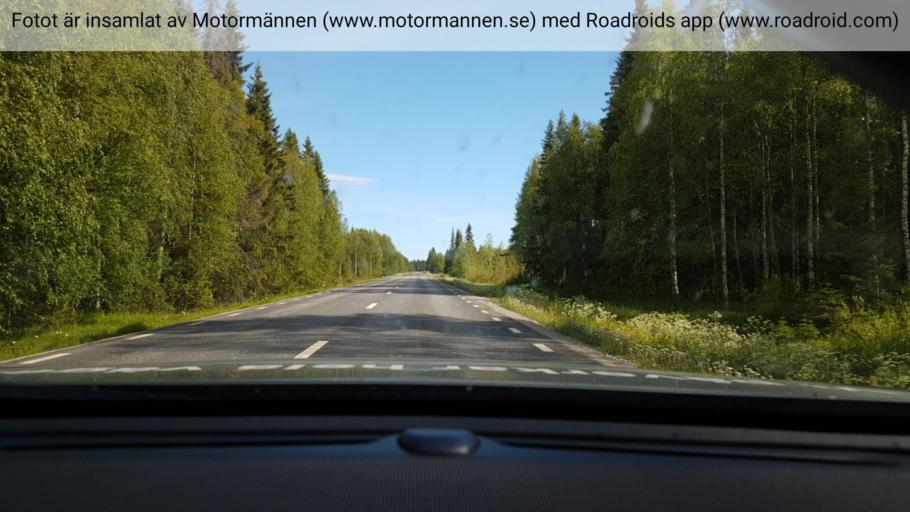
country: SE
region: Vaesterbotten
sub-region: Lycksele Kommun
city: Soderfors
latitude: 64.8230
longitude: 18.0594
